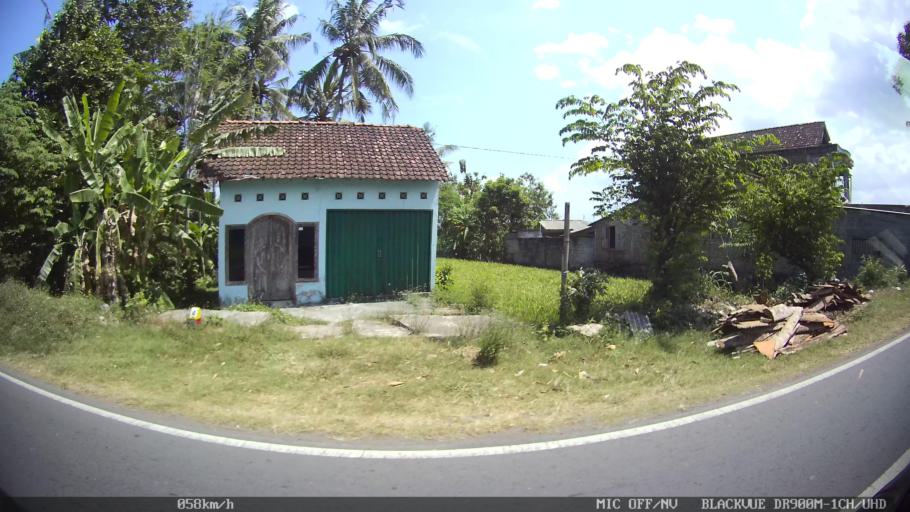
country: ID
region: Daerah Istimewa Yogyakarta
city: Pandak
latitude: -7.9184
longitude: 110.2836
